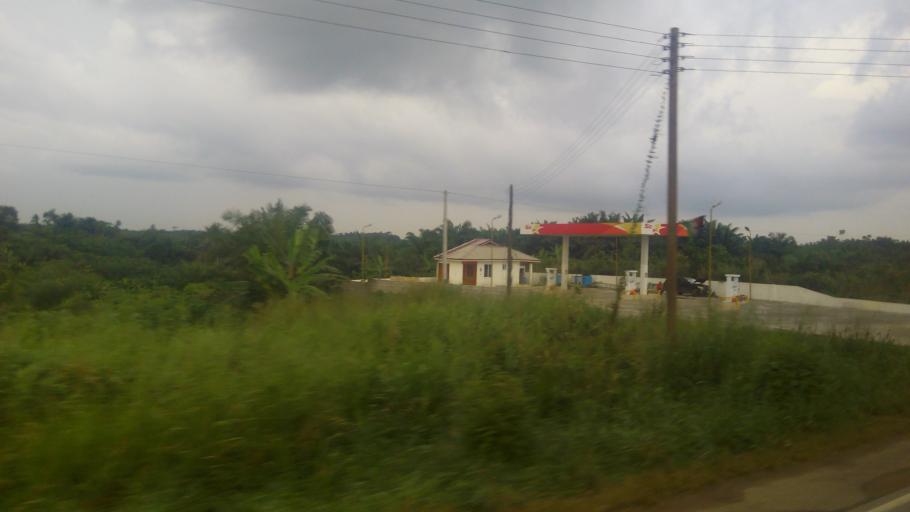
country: GH
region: Western
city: Takoradi
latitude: 4.8966
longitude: -1.9327
